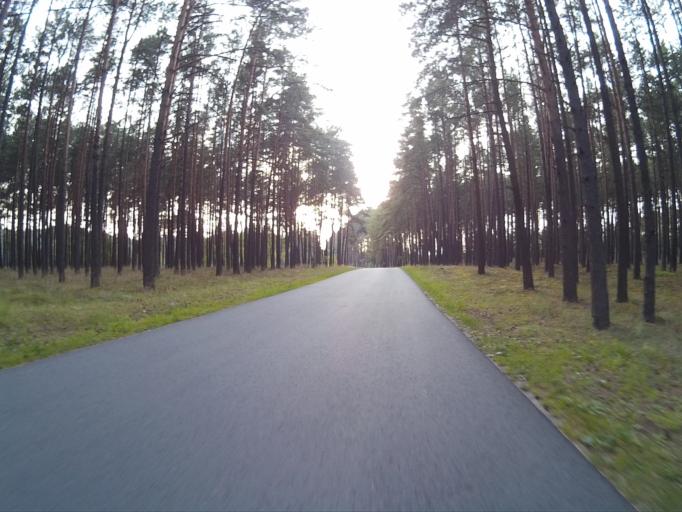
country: PL
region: Pomeranian Voivodeship
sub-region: Powiat chojnicki
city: Czersk
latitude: 53.7217
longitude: 17.9394
